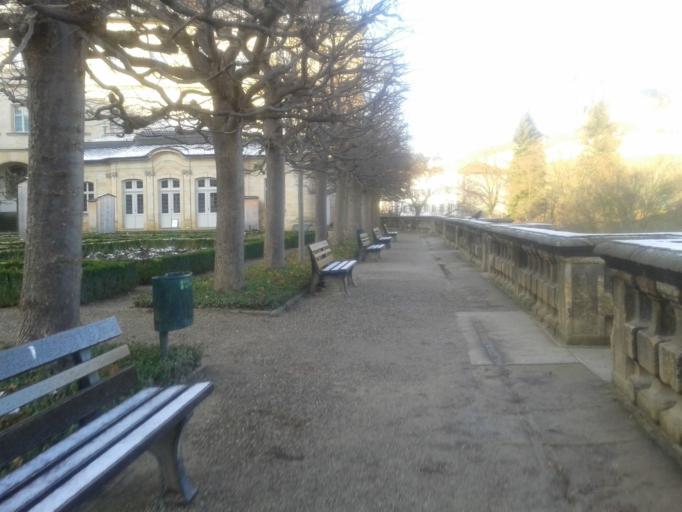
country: DE
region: Bavaria
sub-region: Upper Franconia
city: Bamberg
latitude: 49.8922
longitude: 10.8819
